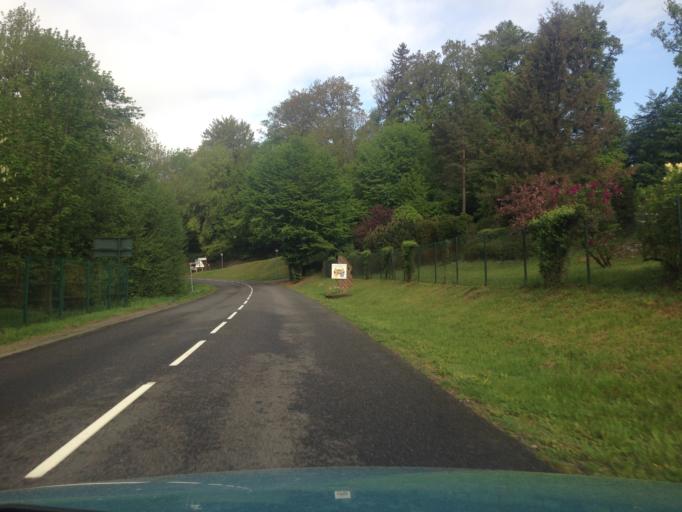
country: FR
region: Alsace
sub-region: Departement du Bas-Rhin
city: Neuwiller-les-Saverne
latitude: 48.8580
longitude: 7.3391
